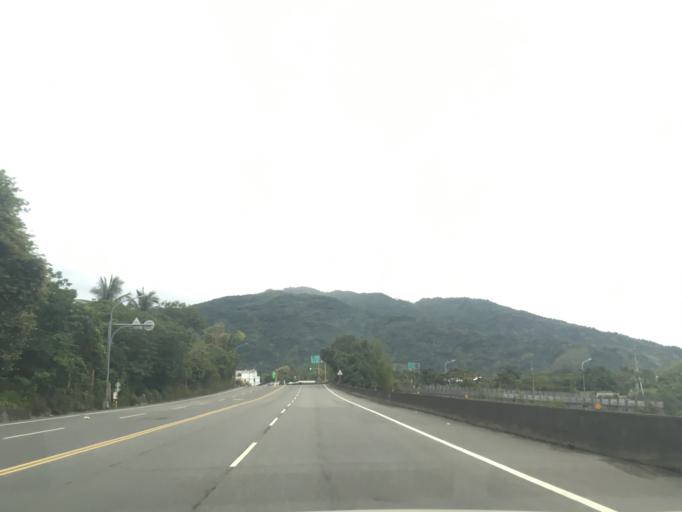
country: TW
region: Taiwan
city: Taitung City
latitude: 22.7545
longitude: 121.0534
